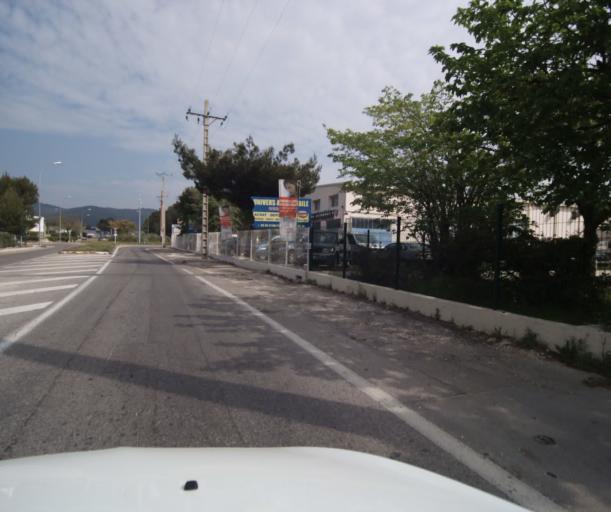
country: FR
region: Provence-Alpes-Cote d'Azur
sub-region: Departement du Var
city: La Farlede
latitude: 43.1463
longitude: 6.0399
